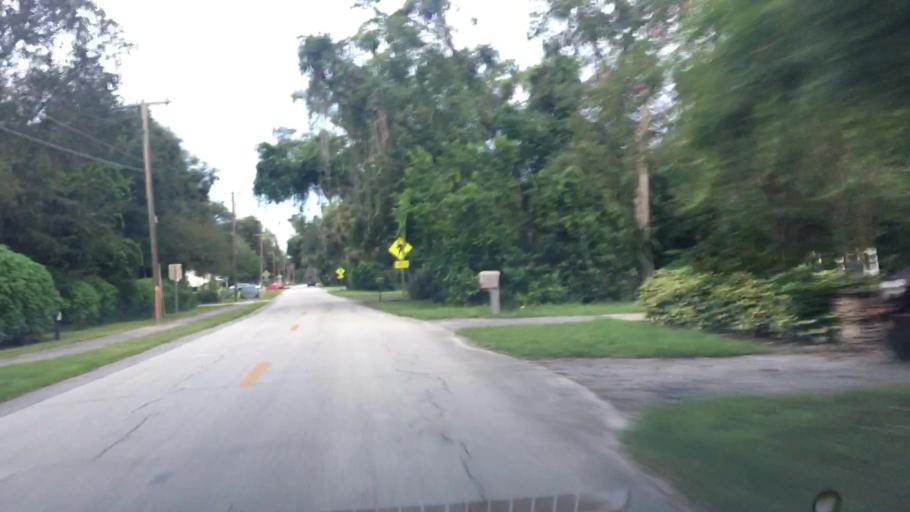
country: US
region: Florida
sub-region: Volusia County
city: DeBary
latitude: 28.8777
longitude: -81.3010
